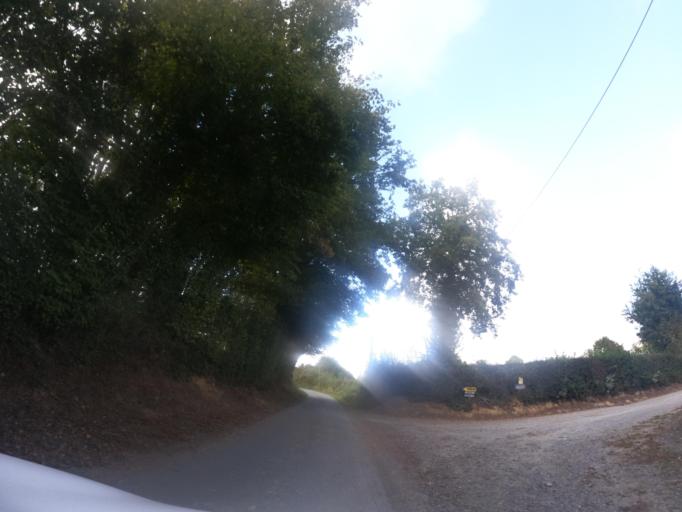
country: FR
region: Poitou-Charentes
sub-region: Departement des Deux-Sevres
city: Courlay
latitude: 46.7805
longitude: -0.6034
